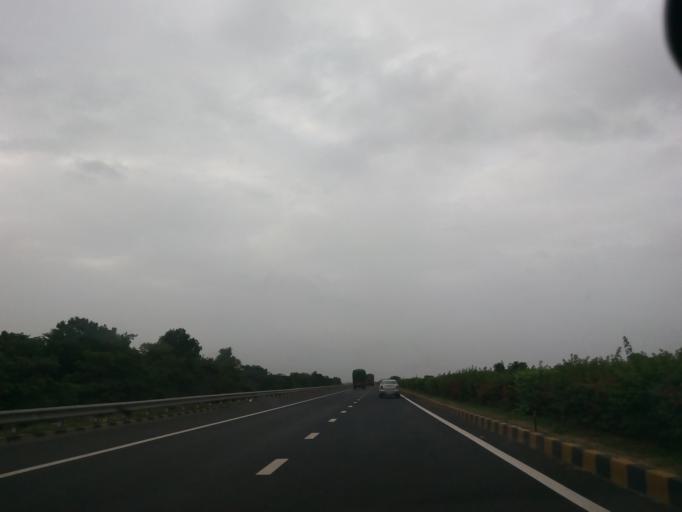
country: IN
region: Gujarat
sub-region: Kheda
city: Chaklasi
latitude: 22.6737
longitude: 72.9128
